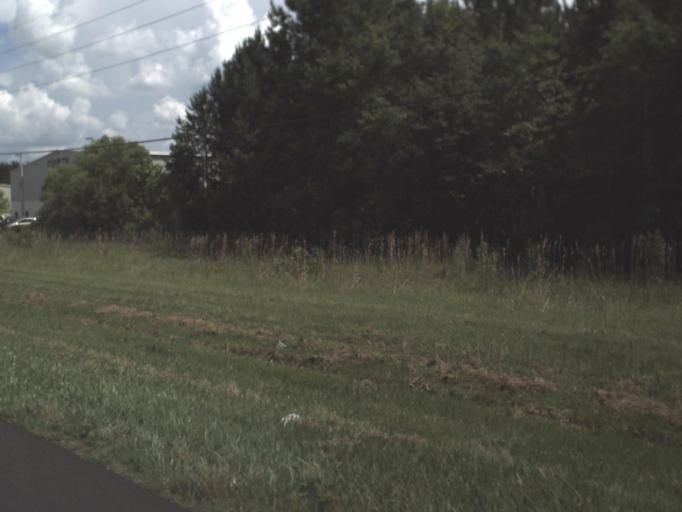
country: US
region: Florida
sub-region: Alachua County
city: Alachua
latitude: 29.7612
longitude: -82.4041
